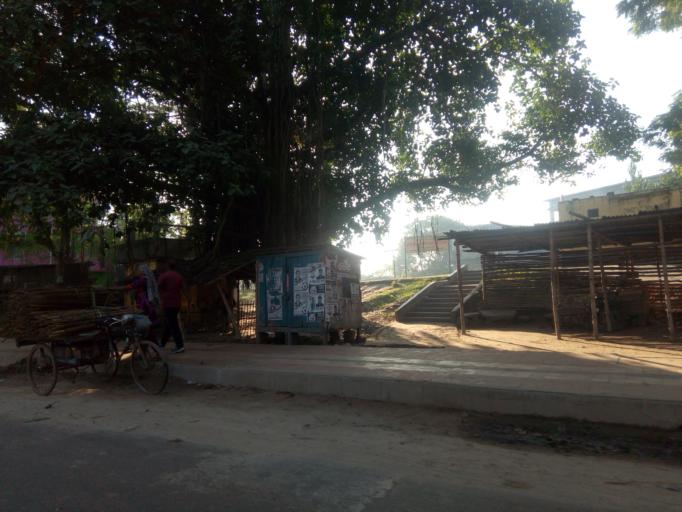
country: BD
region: Rajshahi
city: Rajshahi
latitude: 24.3603
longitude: 88.6241
